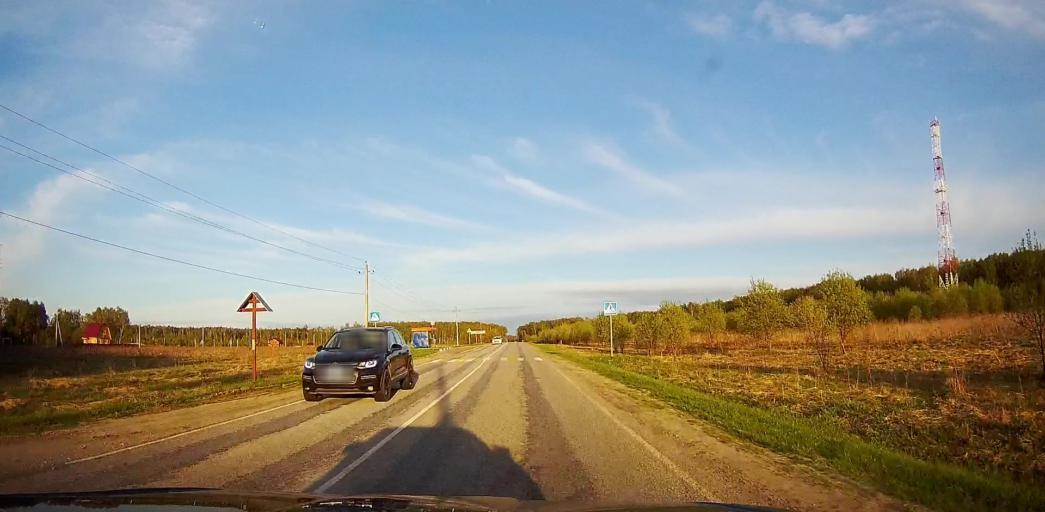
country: RU
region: Moskovskaya
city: Meshcherino
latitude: 55.2306
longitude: 38.3751
